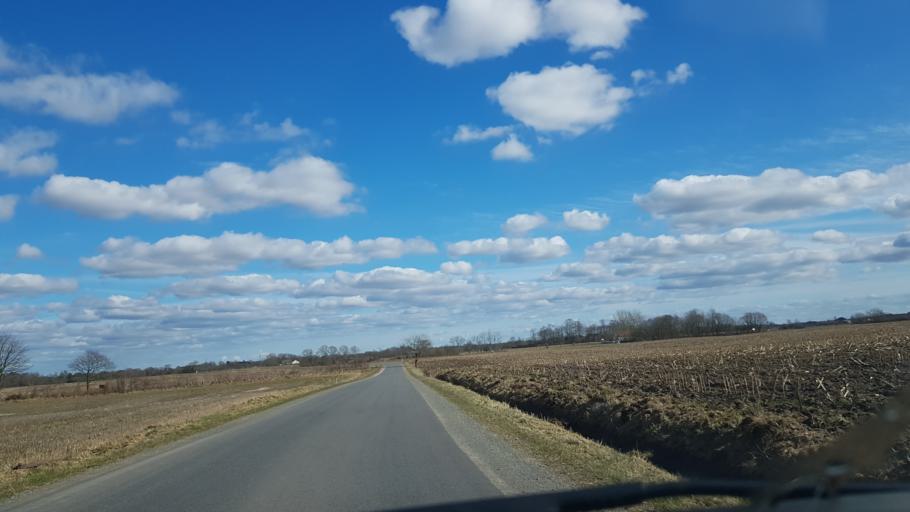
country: DK
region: South Denmark
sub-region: Kolding Kommune
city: Vamdrup
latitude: 55.4064
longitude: 9.2045
